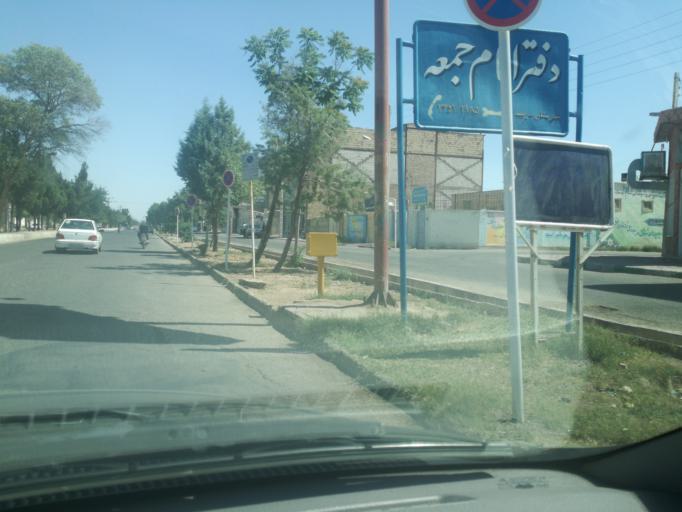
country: IR
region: Razavi Khorasan
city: Sarakhs
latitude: 36.5427
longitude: 61.1641
